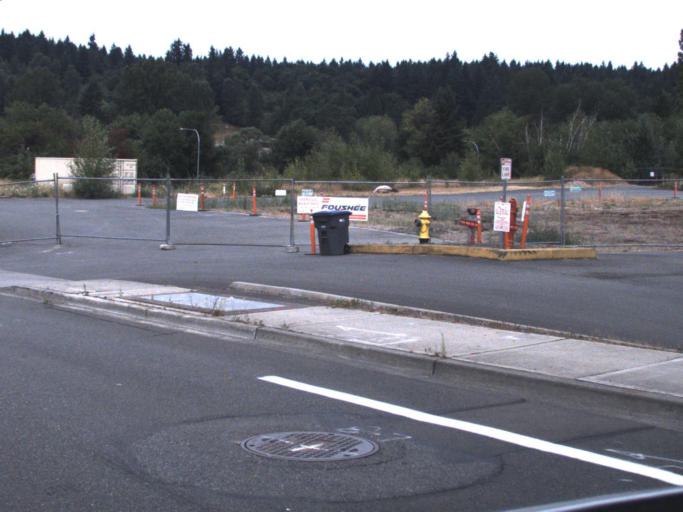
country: US
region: Washington
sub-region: King County
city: Redmond
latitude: 47.7100
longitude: -122.1319
